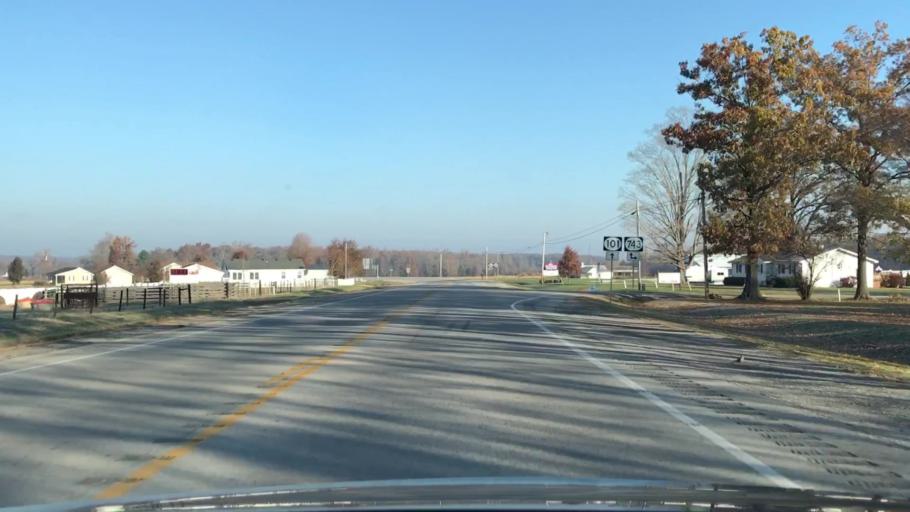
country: US
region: Kentucky
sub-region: Edmonson County
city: Brownsville
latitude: 37.1130
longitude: -86.2292
